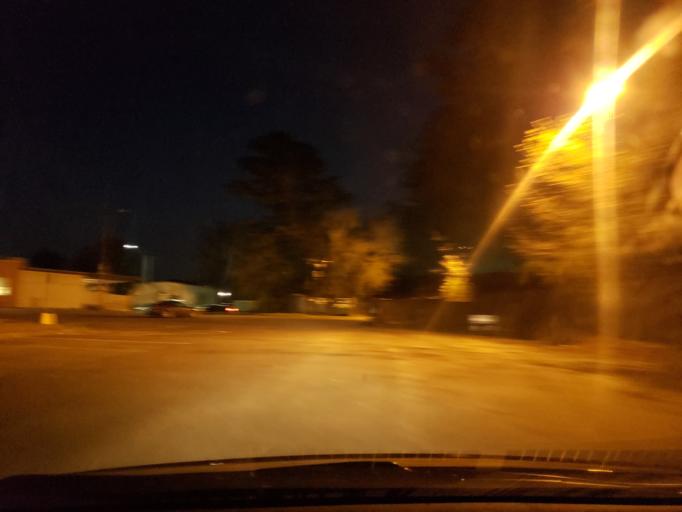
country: US
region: Georgia
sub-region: Chatham County
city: Montgomery
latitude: 31.9778
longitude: -81.1600
